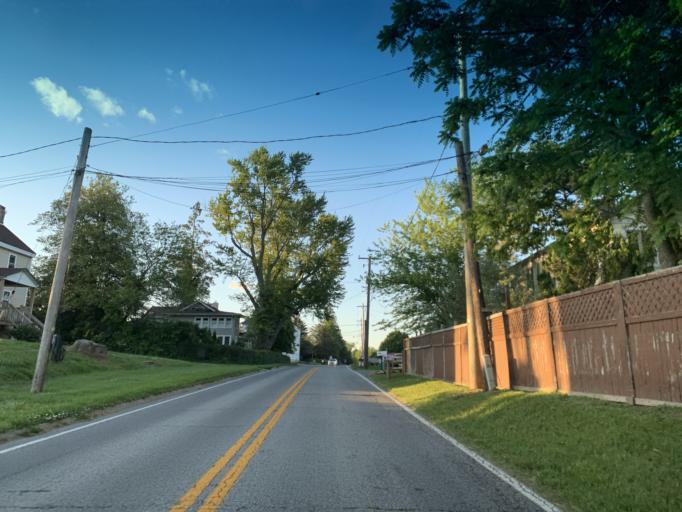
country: US
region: Pennsylvania
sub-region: Chester County
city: West Grove
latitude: 39.7212
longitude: -75.8753
